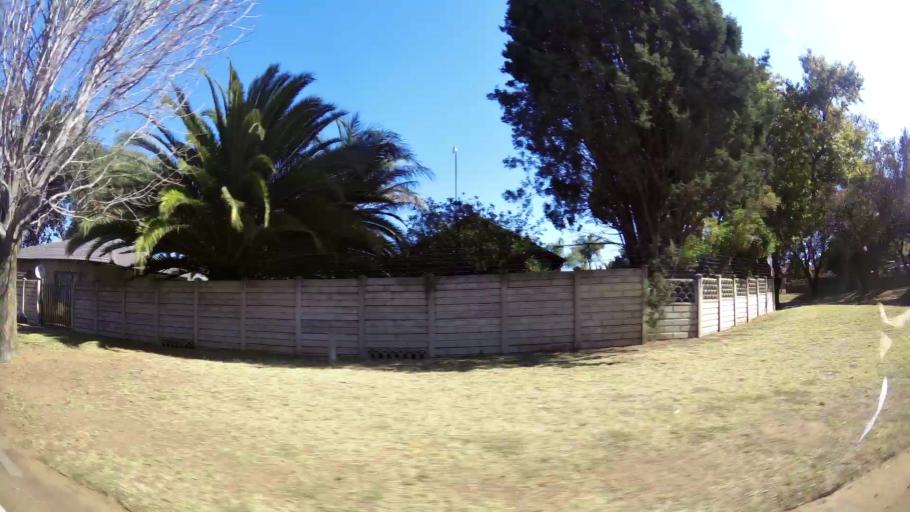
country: ZA
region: Mpumalanga
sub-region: Nkangala District Municipality
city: Witbank
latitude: -25.8311
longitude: 29.2432
